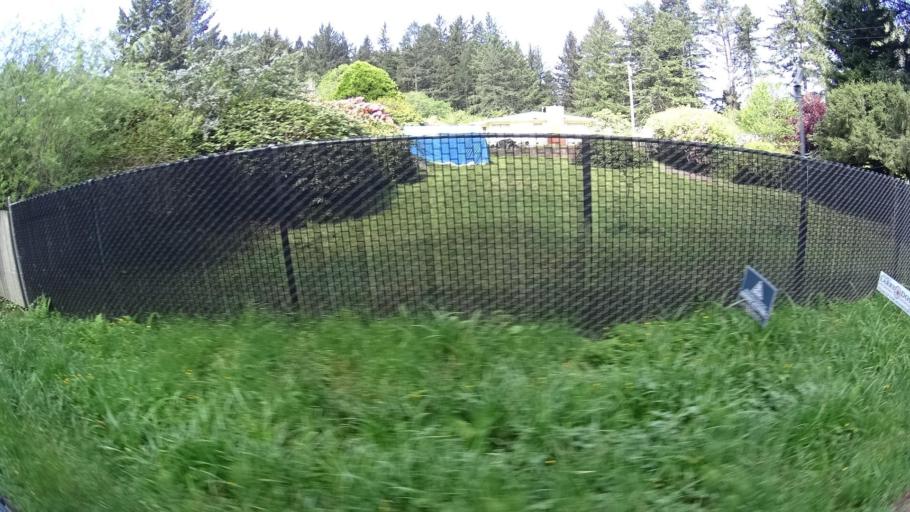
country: US
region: California
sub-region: Humboldt County
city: McKinleyville
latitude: 40.9255
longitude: -124.0816
